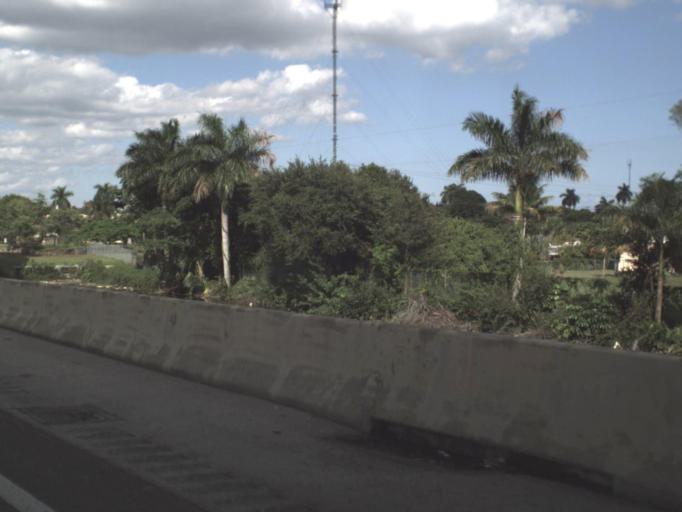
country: US
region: Florida
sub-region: Miami-Dade County
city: Lake Lucerne
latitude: 25.9593
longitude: -80.2291
